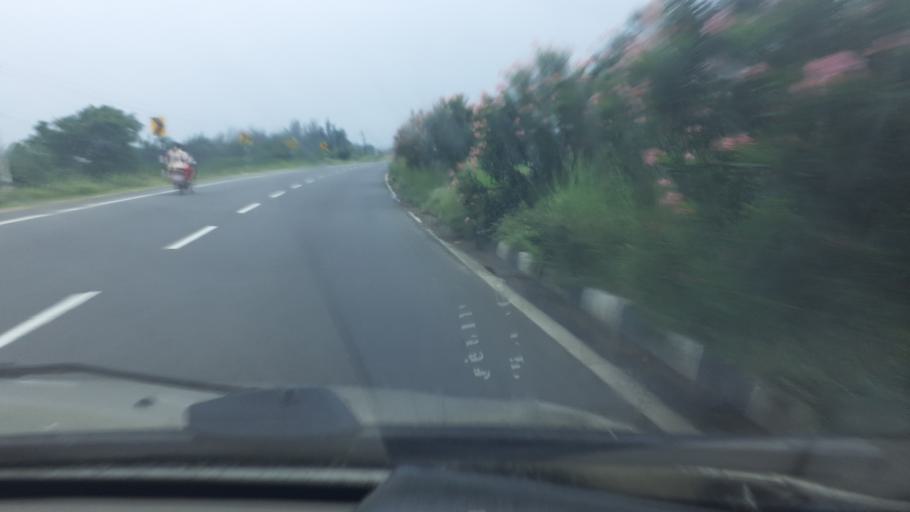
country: IN
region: Tamil Nadu
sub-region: Virudhunagar
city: Virudunagar
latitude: 9.6330
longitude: 77.9607
